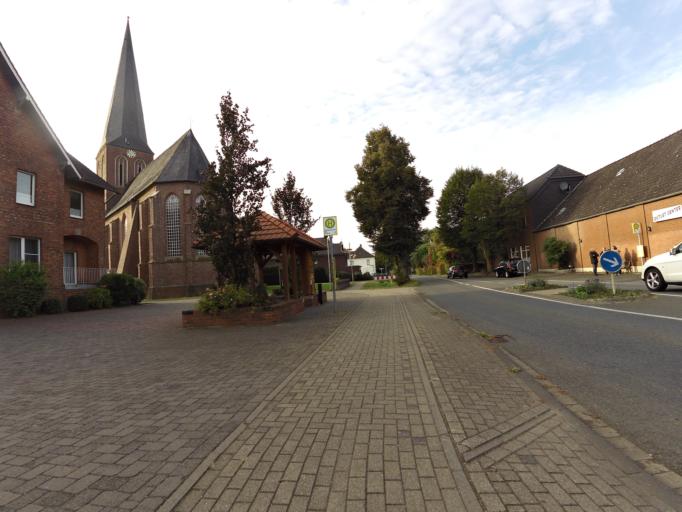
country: DE
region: North Rhine-Westphalia
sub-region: Regierungsbezirk Dusseldorf
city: Mehrhoog
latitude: 51.7919
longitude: 6.5250
